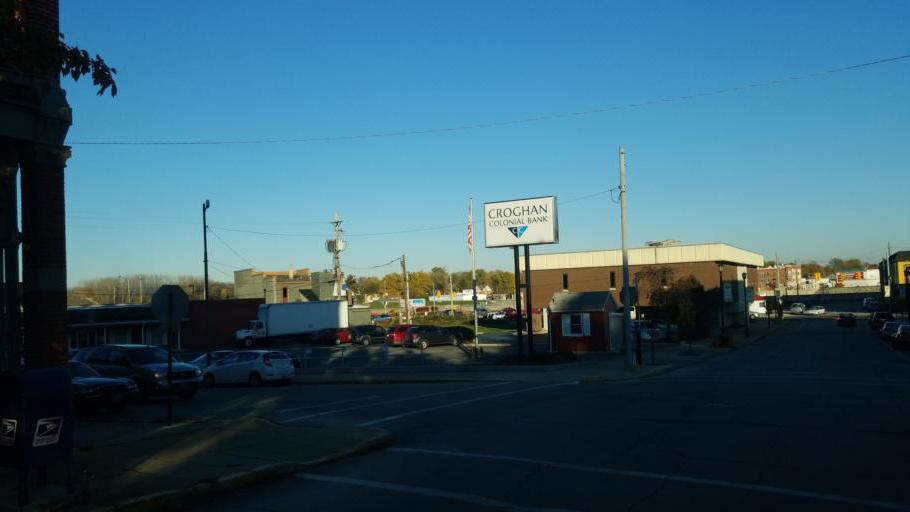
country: US
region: Ohio
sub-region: Sandusky County
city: Fremont
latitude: 41.3465
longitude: -83.1149
